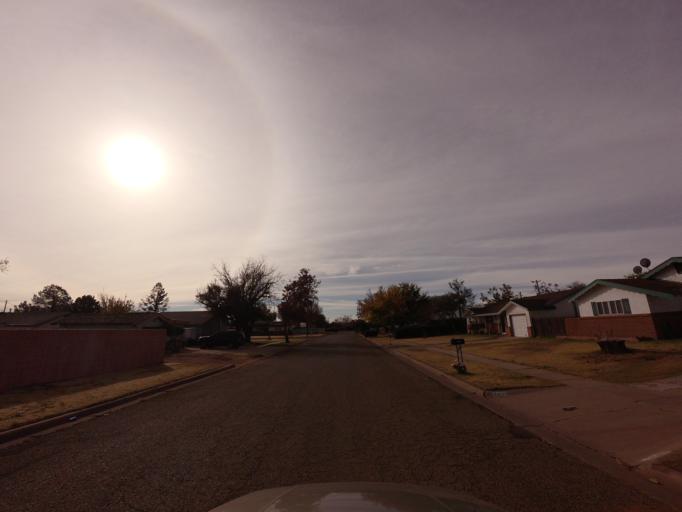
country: US
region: New Mexico
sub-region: Curry County
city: Clovis
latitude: 34.4252
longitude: -103.2171
